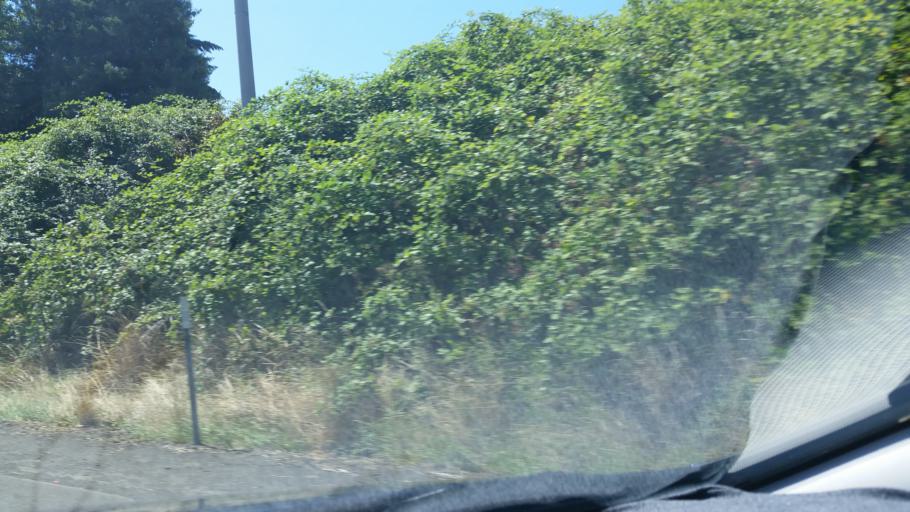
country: US
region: Oregon
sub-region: Clackamas County
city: Wilsonville
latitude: 45.2839
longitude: -122.7698
